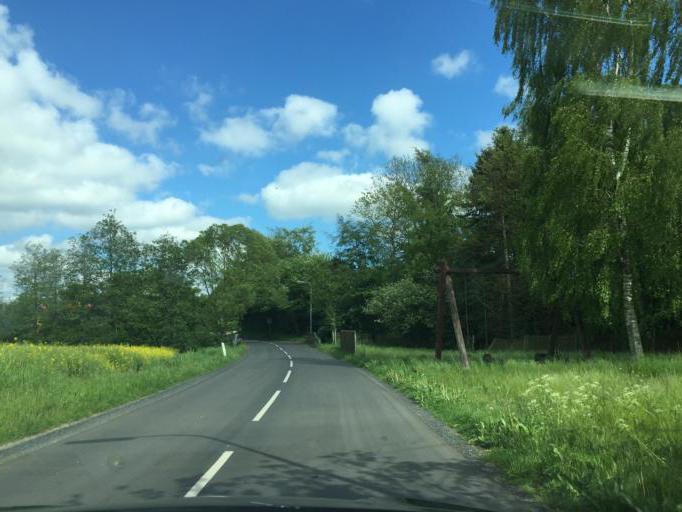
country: DK
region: South Denmark
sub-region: Odense Kommune
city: Bellinge
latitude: 55.3488
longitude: 10.2620
